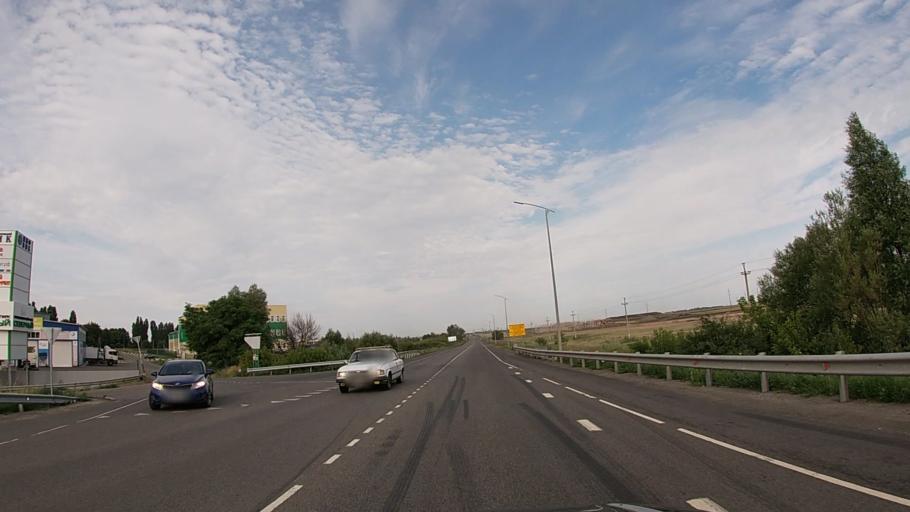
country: RU
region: Belgorod
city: Severnyy
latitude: 50.6675
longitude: 36.5526
